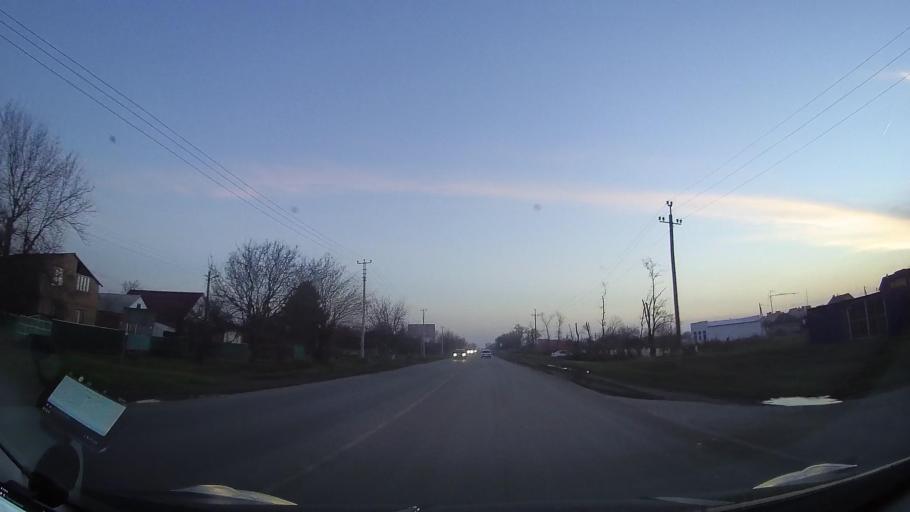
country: RU
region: Rostov
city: Zernograd
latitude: 46.8422
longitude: 40.2994
